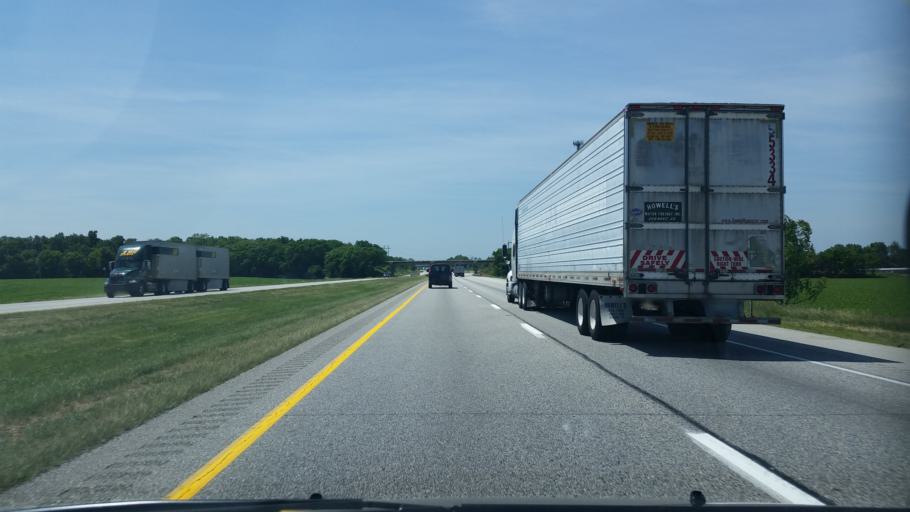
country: US
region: Pennsylvania
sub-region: Franklin County
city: Chambersburg
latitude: 39.8729
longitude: -77.6795
